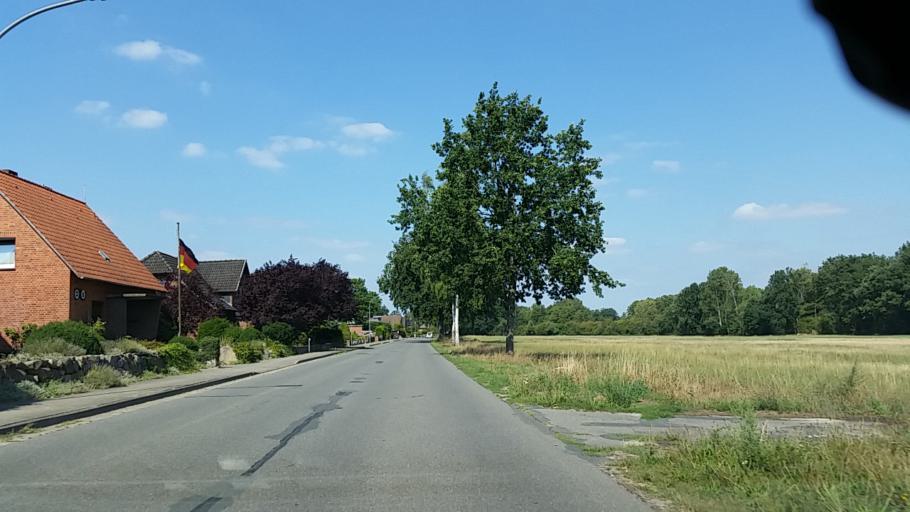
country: DE
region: Lower Saxony
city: Jelmstorf
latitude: 53.1003
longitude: 10.5525
